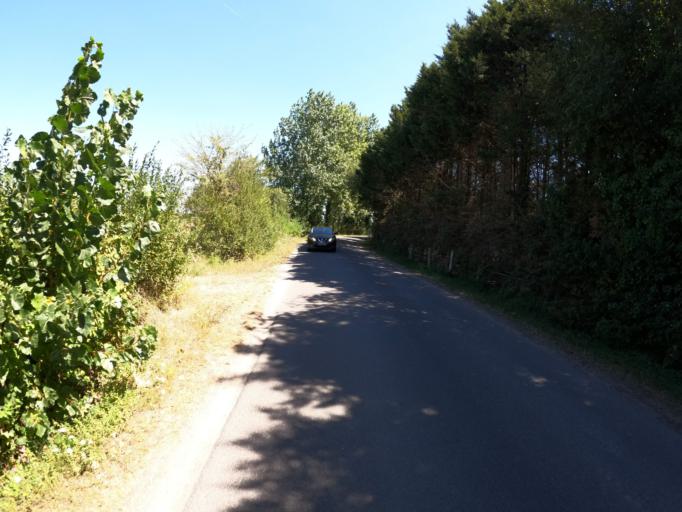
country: FR
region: Pays de la Loire
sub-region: Departement de la Vendee
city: Saint-Jean-de-Monts
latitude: 46.8025
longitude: -2.0809
